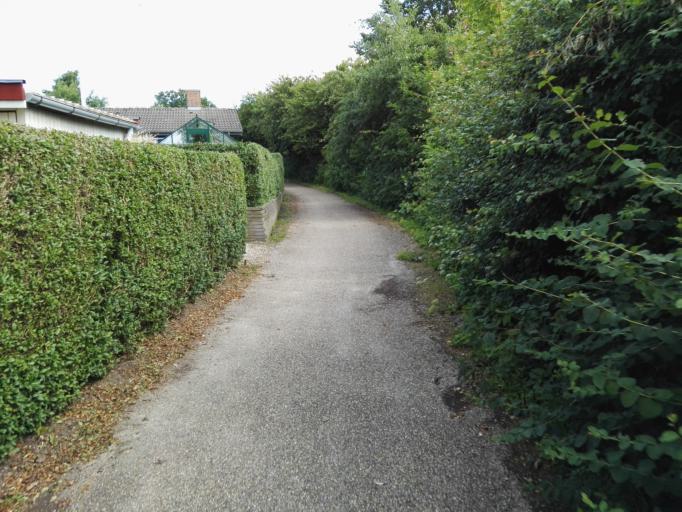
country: DK
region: Capital Region
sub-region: Herlev Kommune
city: Herlev
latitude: 55.7361
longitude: 12.4094
